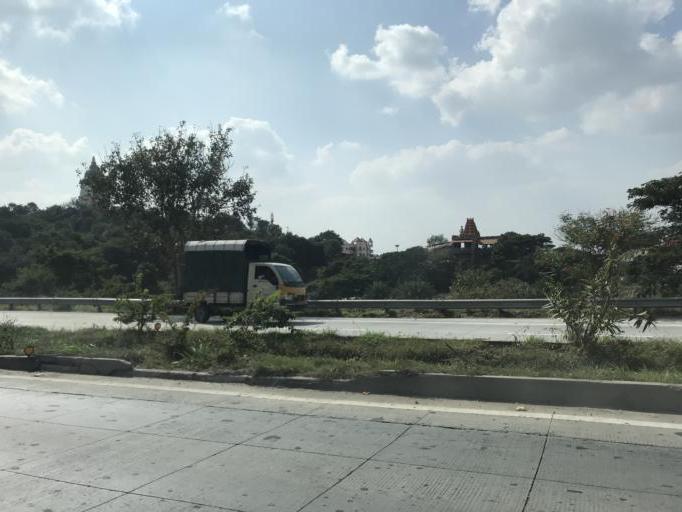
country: IN
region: Karnataka
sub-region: Bangalore Urban
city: Bangalore
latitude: 12.9143
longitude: 77.5314
